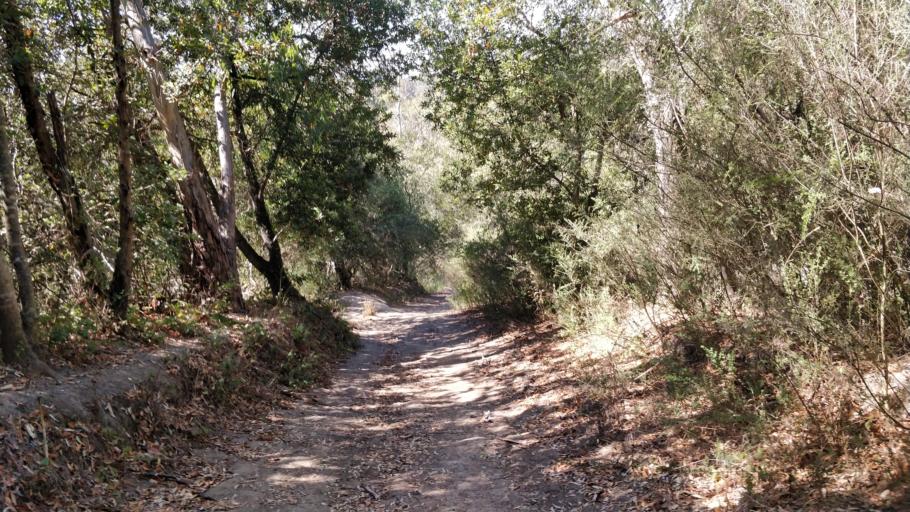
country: US
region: California
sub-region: Alameda County
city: Berkeley
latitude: 37.8740
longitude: -122.2274
